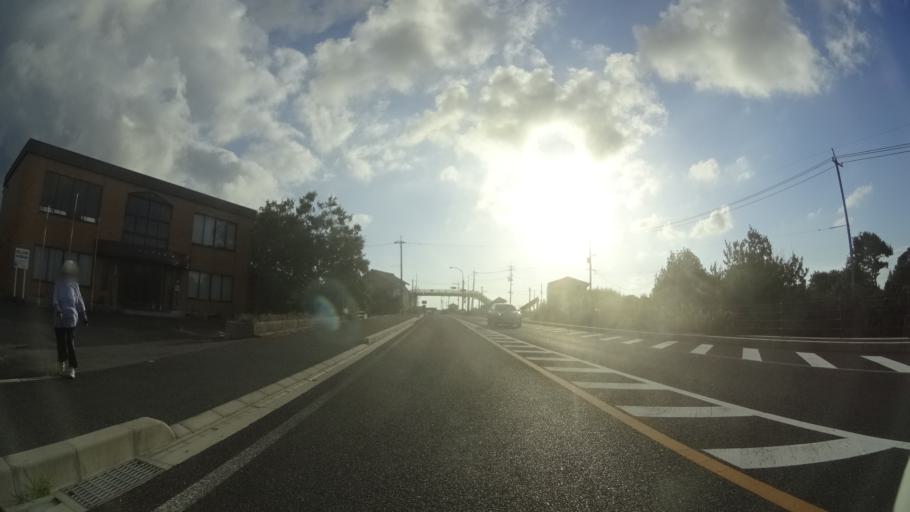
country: JP
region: Tottori
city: Yonago
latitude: 35.5220
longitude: 133.5705
